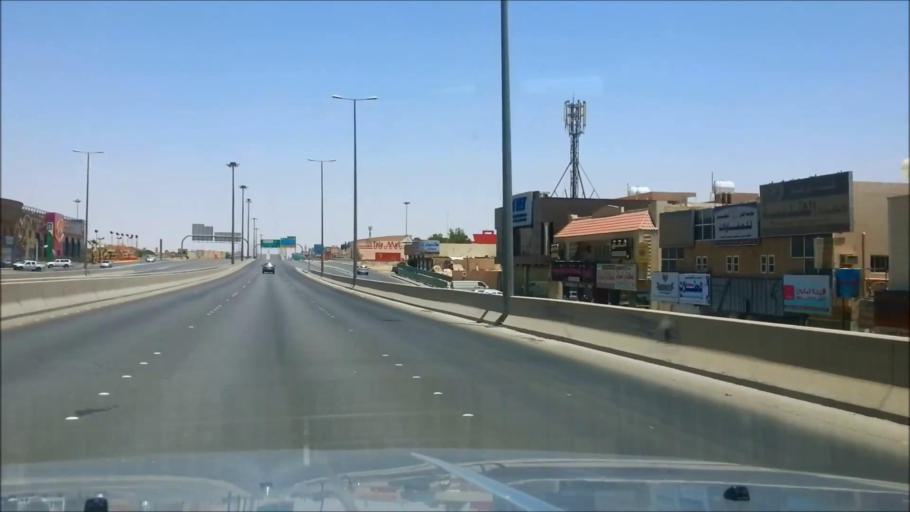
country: SA
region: Ar Riyad
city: Riyadh
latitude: 24.7649
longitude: 46.6711
